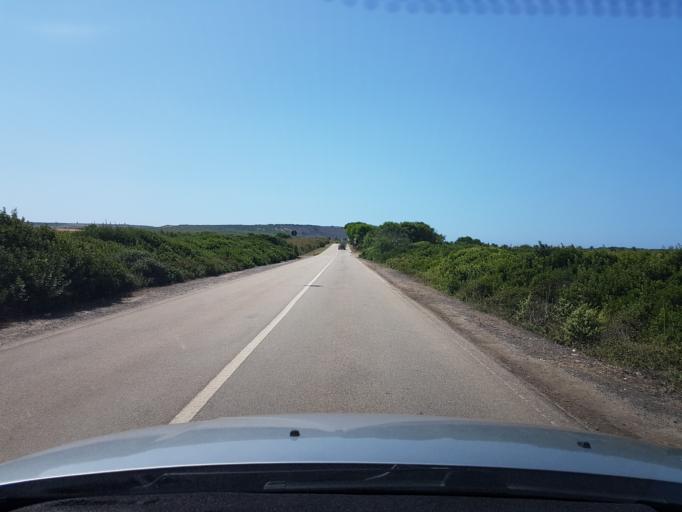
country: IT
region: Sardinia
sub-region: Provincia di Oristano
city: Riola Sardo
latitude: 40.0403
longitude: 8.4083
